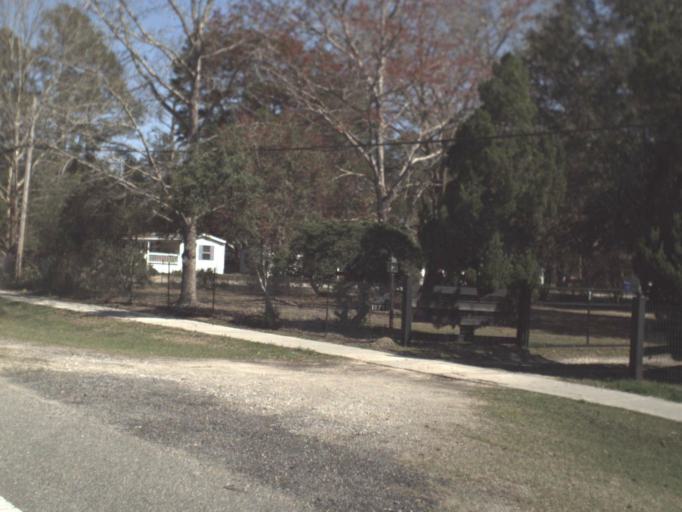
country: US
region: Florida
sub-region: Calhoun County
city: Blountstown
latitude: 30.4722
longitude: -85.0448
